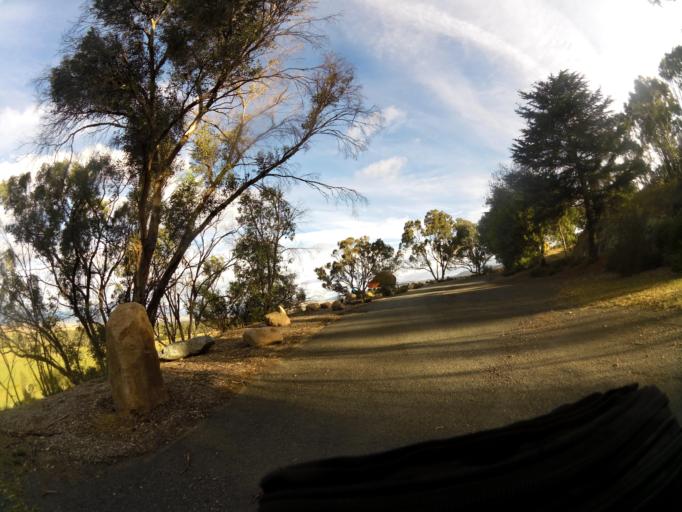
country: AU
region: New South Wales
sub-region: Greater Hume Shire
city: Holbrook
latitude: -36.0109
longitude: 147.9084
